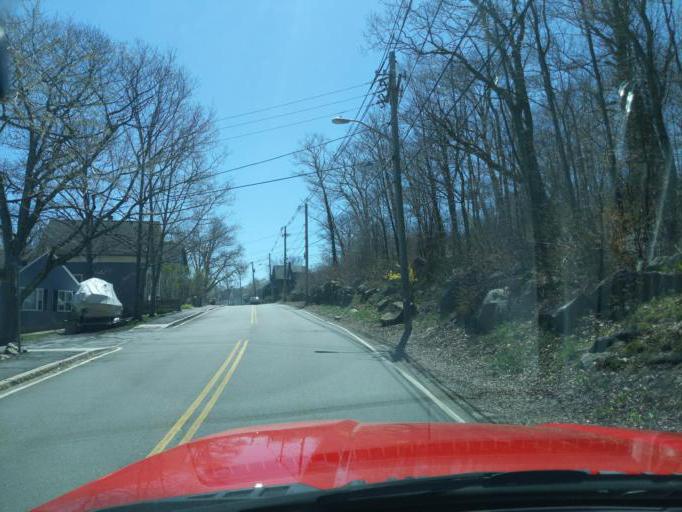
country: US
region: Massachusetts
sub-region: Essex County
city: Rockport
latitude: 42.6599
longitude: -70.6268
